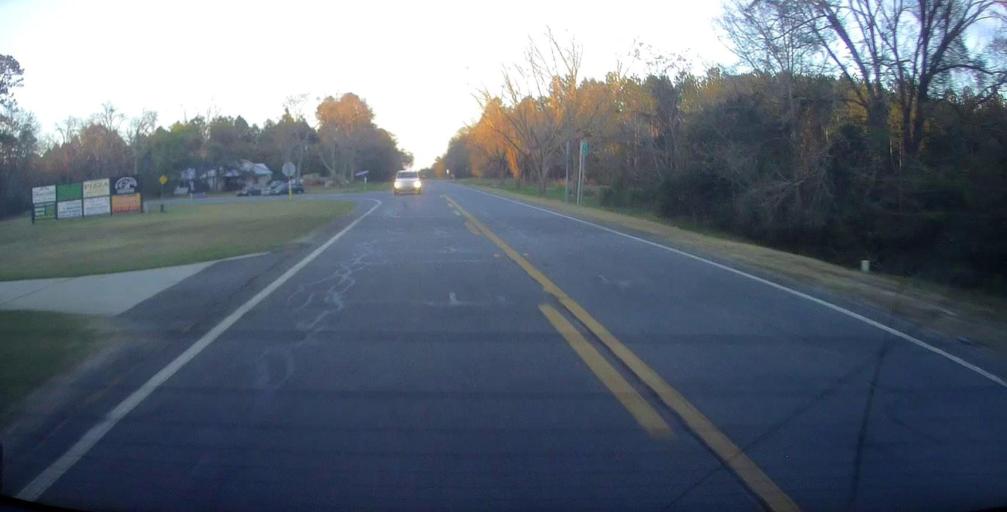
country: US
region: Georgia
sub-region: Dodge County
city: Eastman
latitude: 32.2633
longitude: -83.1325
